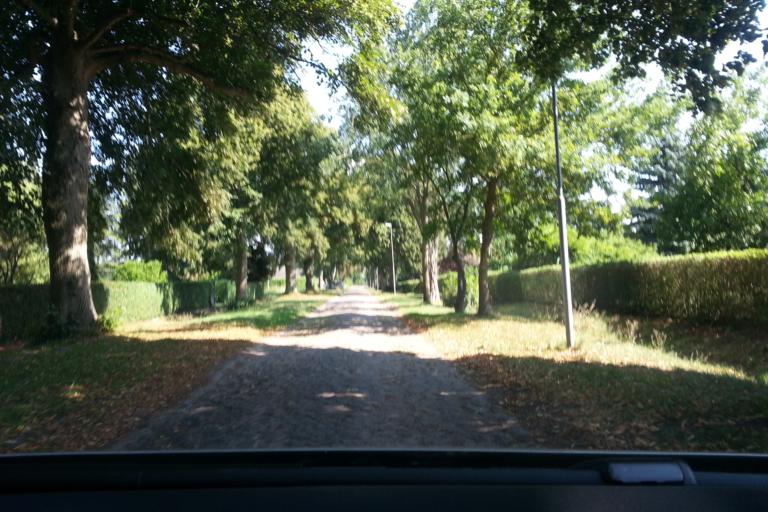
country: DE
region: Mecklenburg-Vorpommern
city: Ducherow
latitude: 53.7150
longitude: 13.7861
